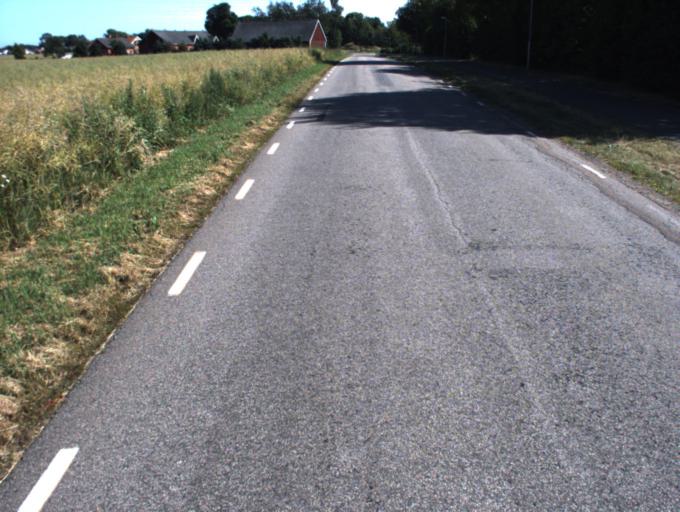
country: SE
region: Skane
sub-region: Helsingborg
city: Barslov
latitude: 56.0119
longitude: 12.8085
